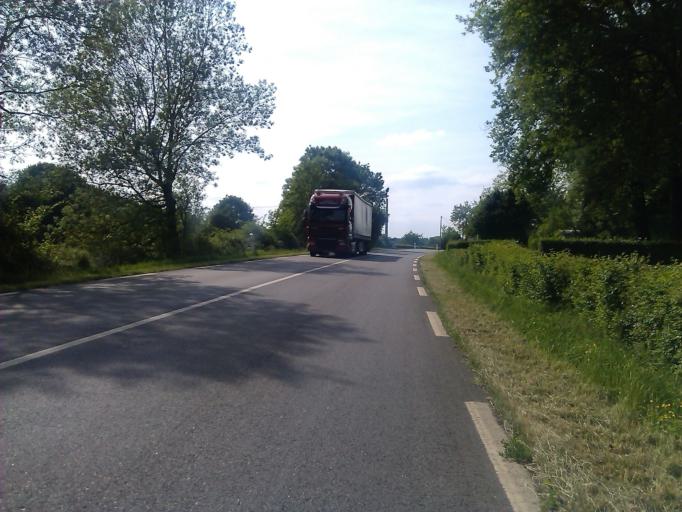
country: FR
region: Centre
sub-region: Departement de l'Indre
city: La Chatre
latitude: 46.5596
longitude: 2.0553
